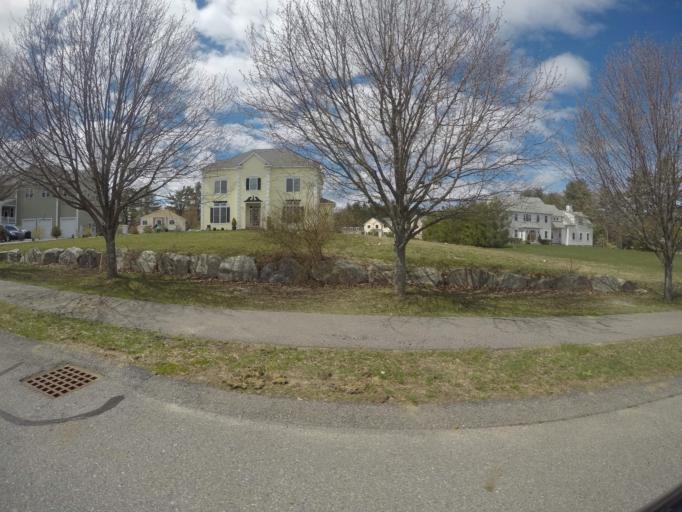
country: US
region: Massachusetts
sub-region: Norfolk County
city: Stoughton
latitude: 42.0776
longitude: -71.0820
